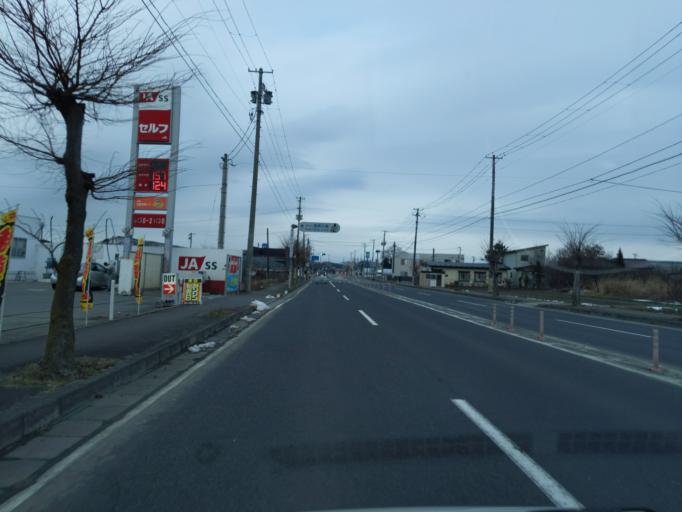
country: JP
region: Iwate
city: Mizusawa
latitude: 39.1741
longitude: 141.1583
